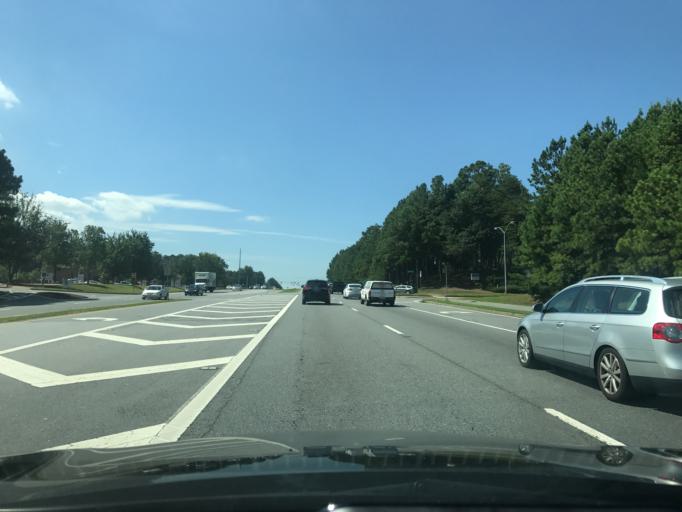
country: US
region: Georgia
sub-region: Gwinnett County
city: Norcross
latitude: 33.9731
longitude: -84.2201
